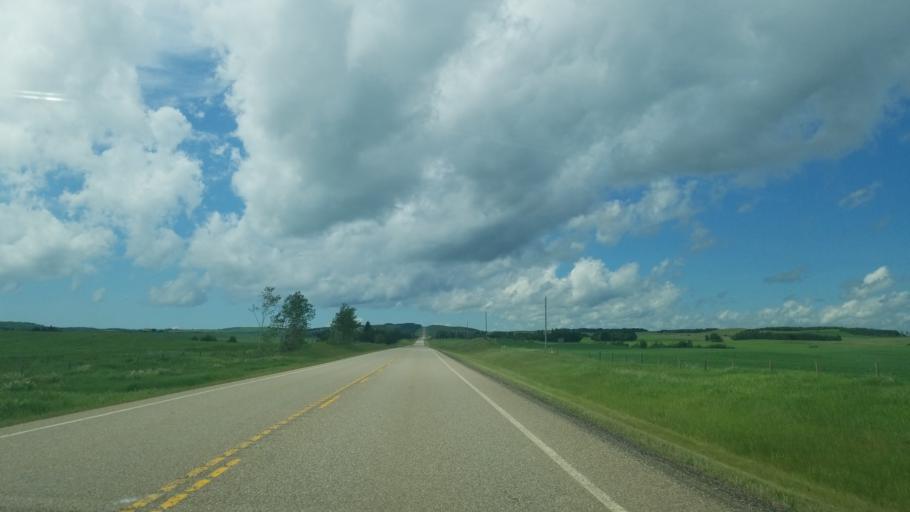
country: CA
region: Saskatchewan
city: Lloydminster
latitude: 53.1617
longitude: -110.1816
